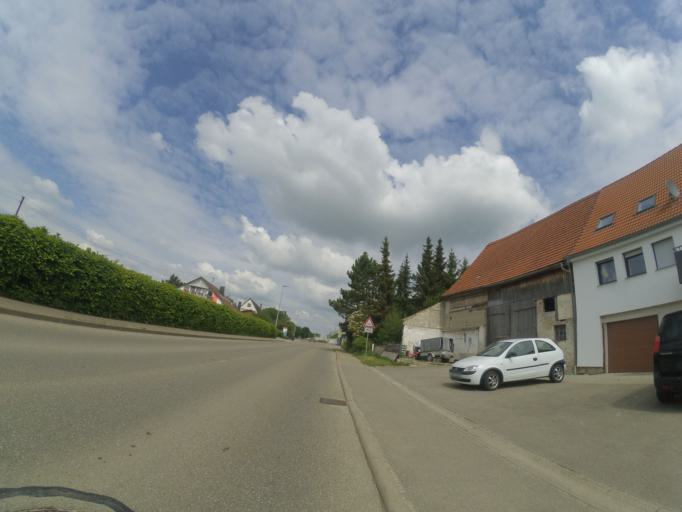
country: DE
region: Baden-Wuerttemberg
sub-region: Tuebingen Region
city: Berghulen
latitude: 48.4592
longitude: 9.7761
